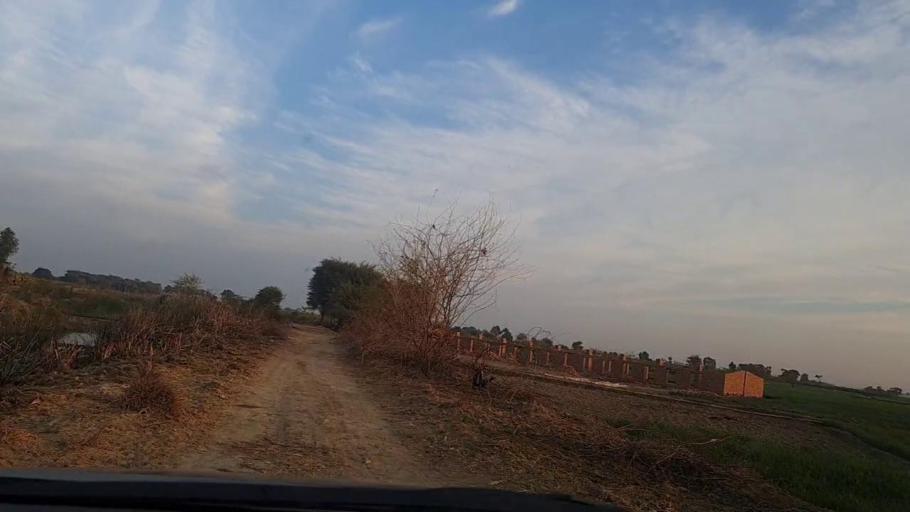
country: PK
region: Sindh
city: Sakrand
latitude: 26.1709
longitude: 68.3490
